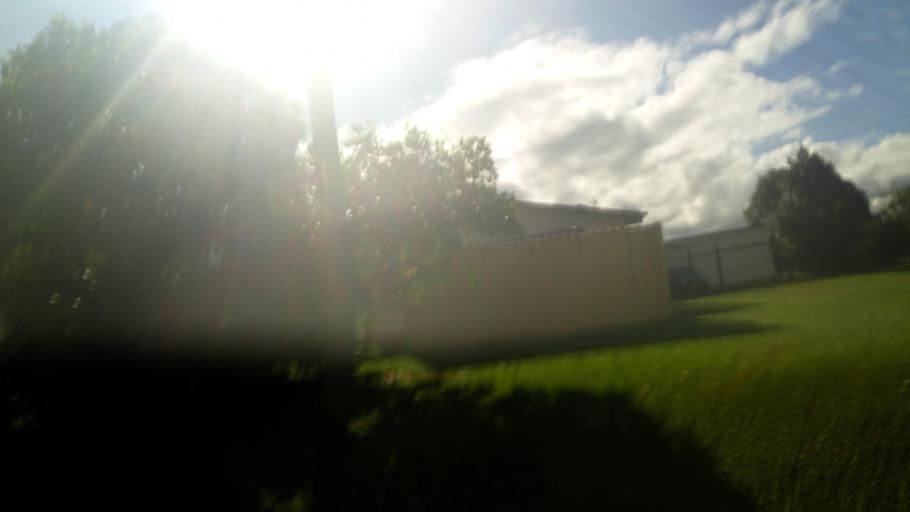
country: AU
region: Queensland
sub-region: Cassowary Coast
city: Innisfail
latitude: -17.5376
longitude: 145.9658
